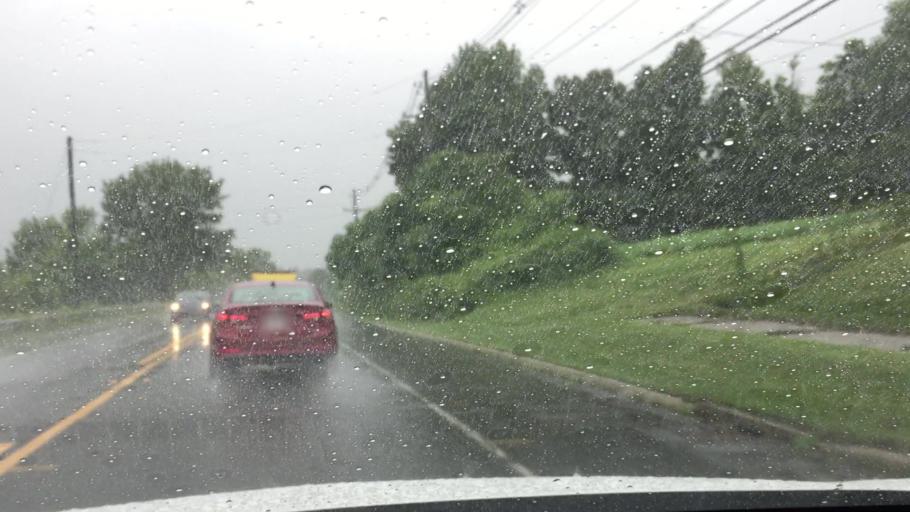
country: US
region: Massachusetts
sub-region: Berkshire County
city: Lanesborough
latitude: 42.5257
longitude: -73.2286
